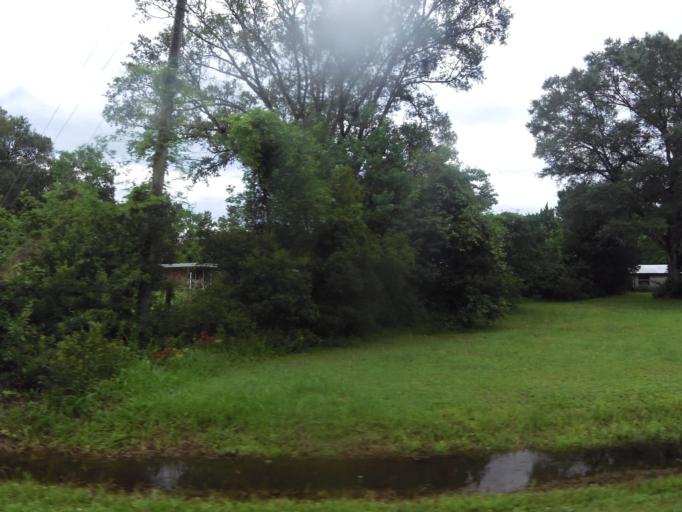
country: US
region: Florida
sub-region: Nassau County
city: Nassau Village-Ratliff
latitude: 30.5085
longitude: -81.8026
